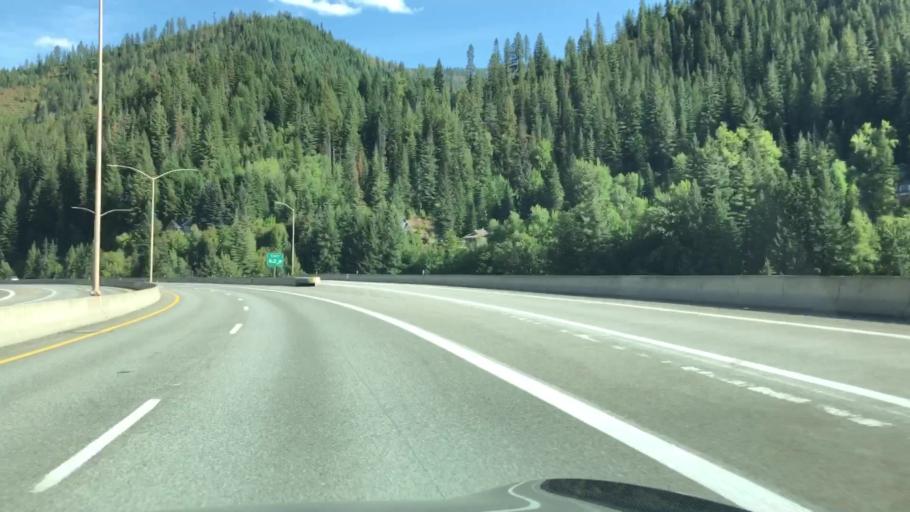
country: US
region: Idaho
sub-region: Shoshone County
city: Wallace
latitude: 47.4722
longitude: -115.9210
